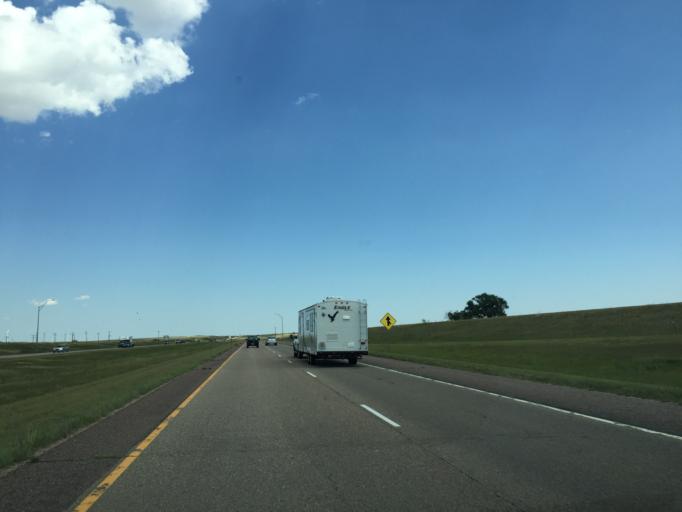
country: US
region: Colorado
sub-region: Lincoln County
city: Hugo
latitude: 39.2788
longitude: -103.3957
